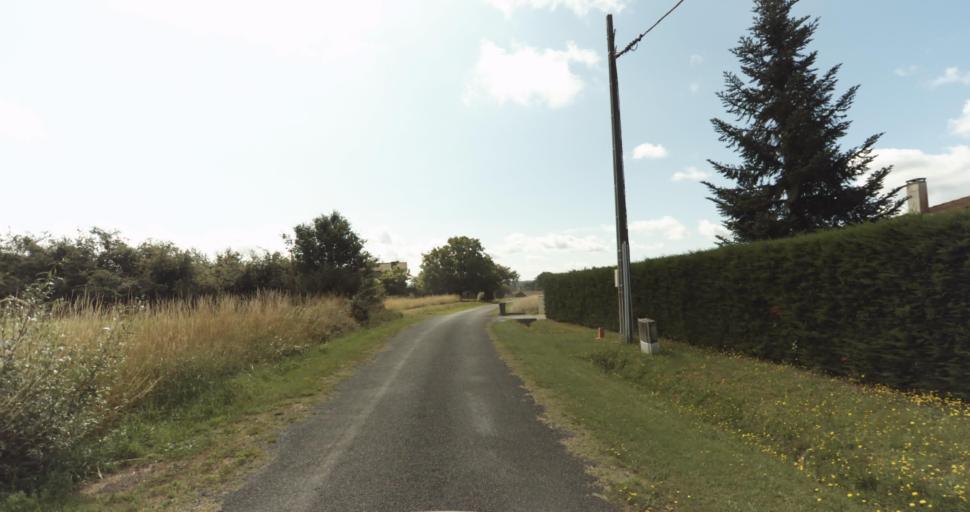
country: FR
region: Aquitaine
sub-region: Departement de la Gironde
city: Bazas
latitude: 44.4375
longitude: -0.2004
